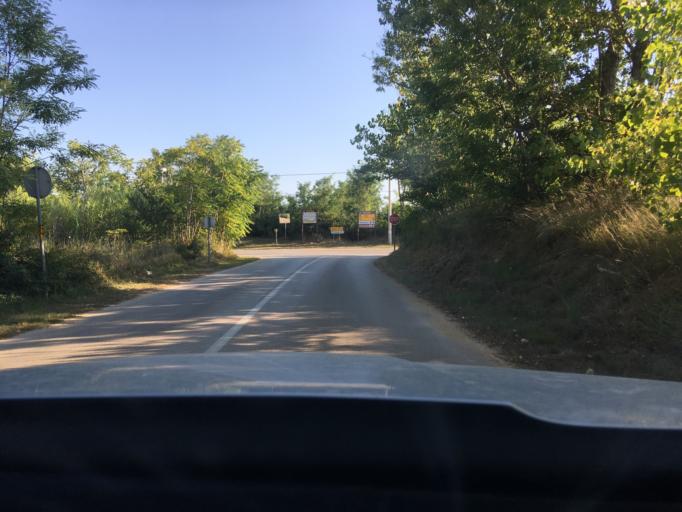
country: HR
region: Zadarska
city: Nin
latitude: 44.2479
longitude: 15.1517
